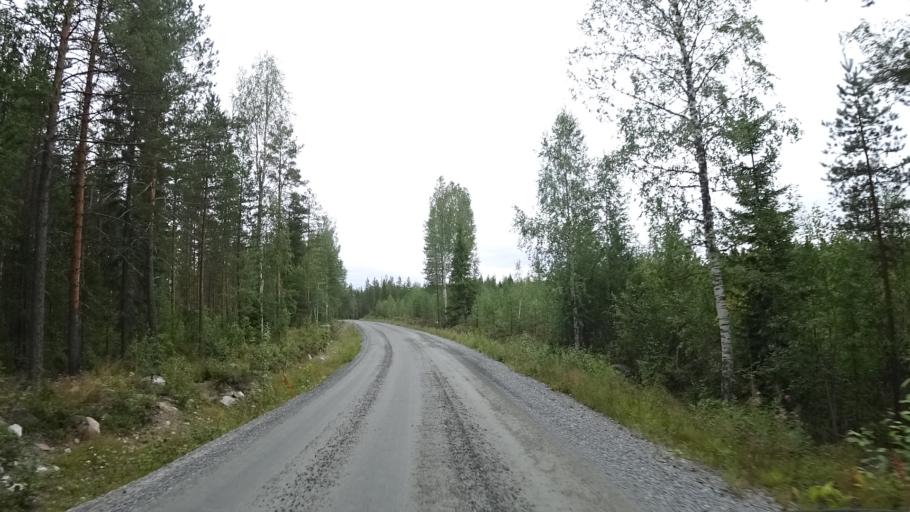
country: FI
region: North Karelia
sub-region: Pielisen Karjala
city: Lieksa
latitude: 63.3671
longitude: 30.3871
